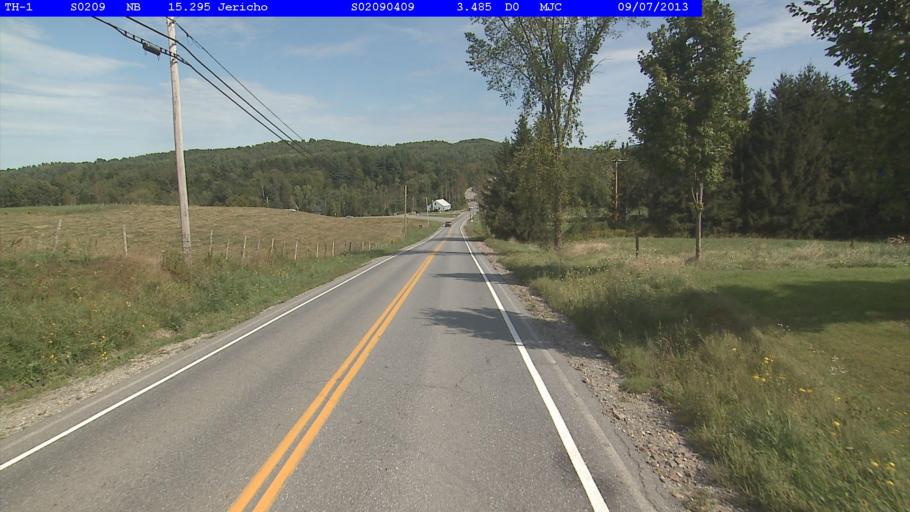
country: US
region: Vermont
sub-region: Chittenden County
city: Jericho
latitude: 44.4778
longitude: -72.9677
